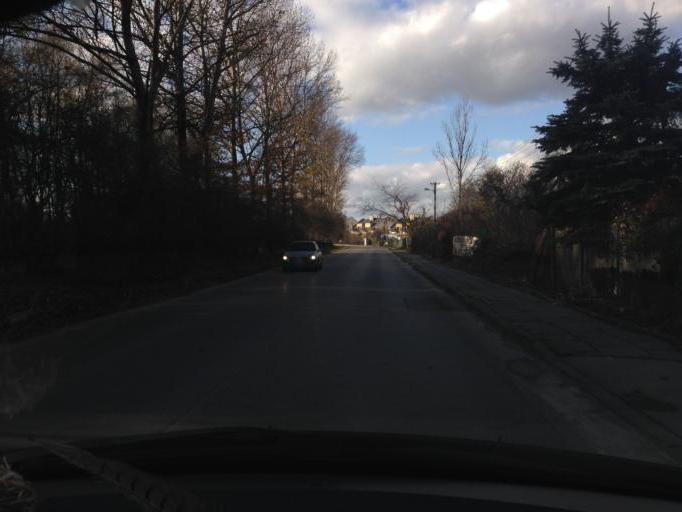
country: PL
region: Lesser Poland Voivodeship
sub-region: Powiat krakowski
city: Rzaska
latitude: 50.0680
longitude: 19.8437
